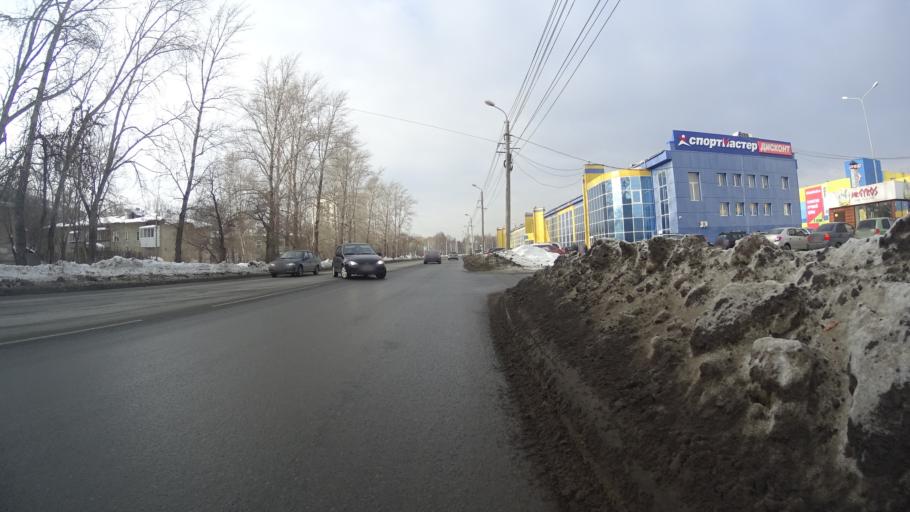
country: RU
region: Chelyabinsk
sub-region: Gorod Chelyabinsk
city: Chelyabinsk
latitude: 55.1256
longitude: 61.3696
